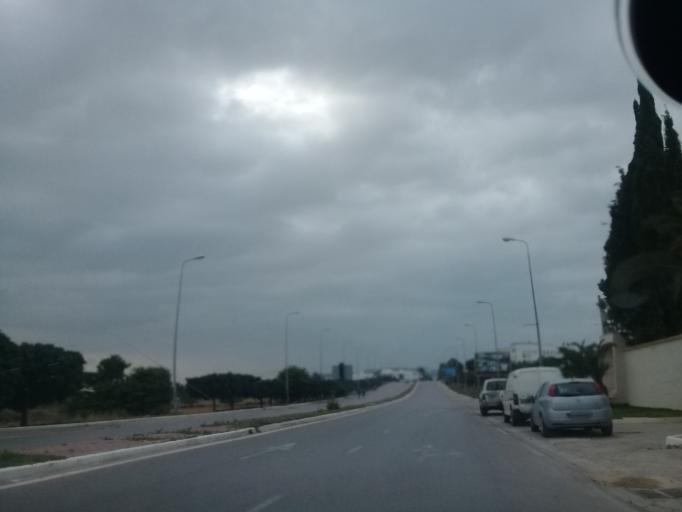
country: TN
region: Tunis
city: Sidi Bou Said
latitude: 36.8683
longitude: 10.3353
